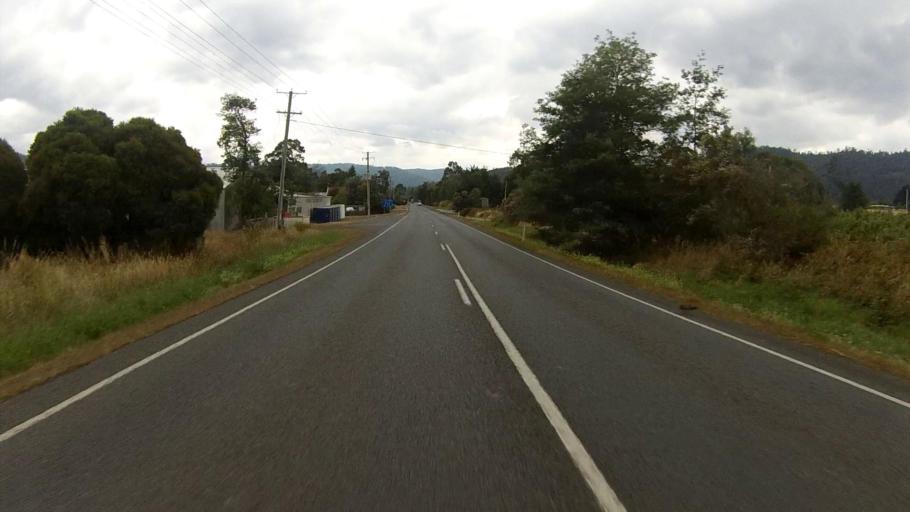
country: AU
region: Tasmania
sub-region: Huon Valley
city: Franklin
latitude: -43.1086
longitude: 147.0354
